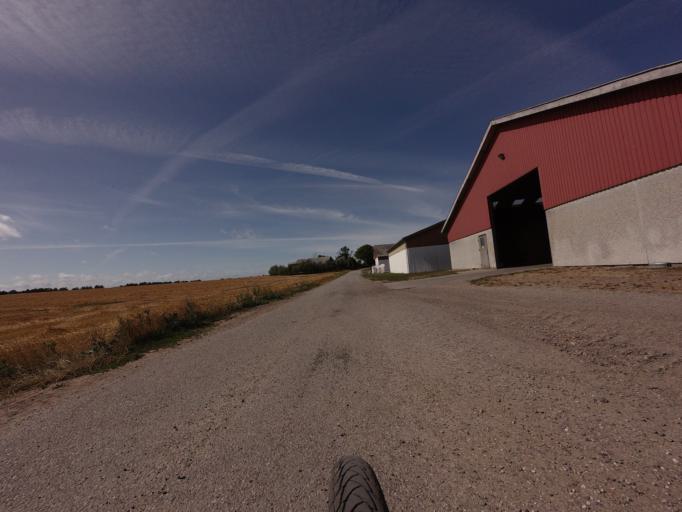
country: DK
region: North Denmark
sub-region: Hjorring Kommune
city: Vra
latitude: 57.3869
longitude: 9.8026
